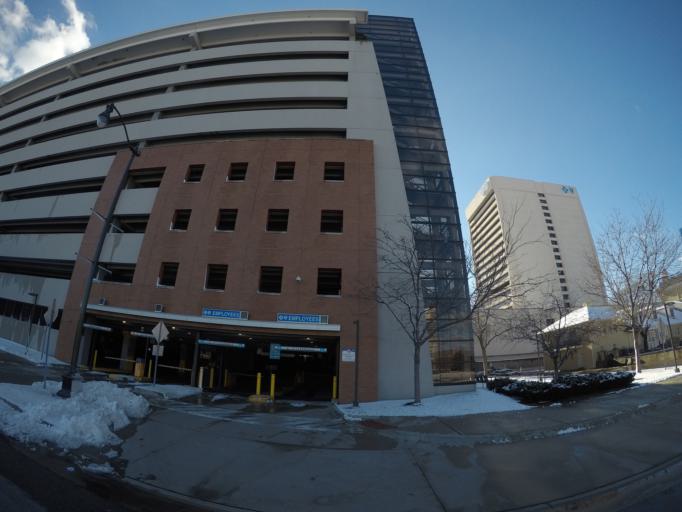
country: US
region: Michigan
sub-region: Wayne County
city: Detroit
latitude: 42.3341
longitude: -83.0374
